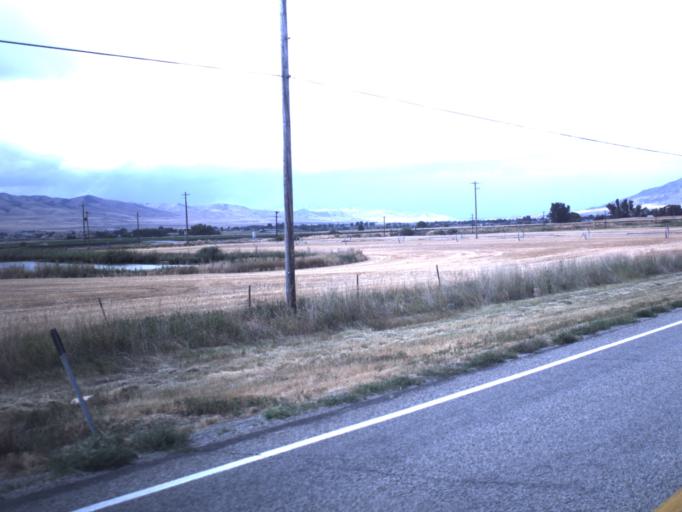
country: US
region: Utah
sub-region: Box Elder County
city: Garland
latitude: 41.7642
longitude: -112.0974
